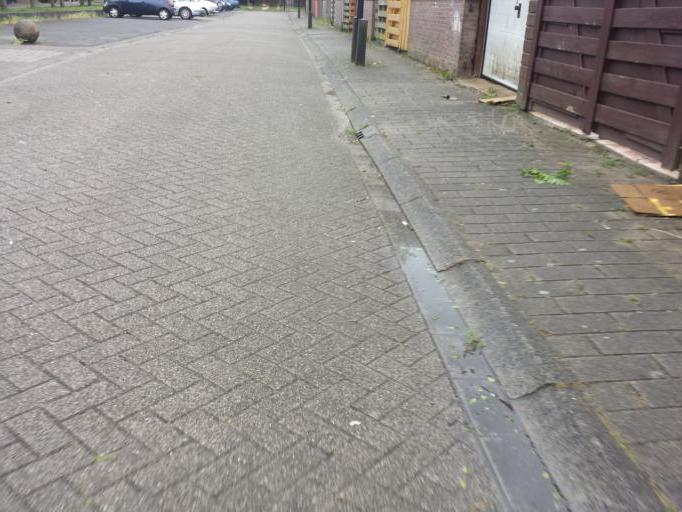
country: NL
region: Flevoland
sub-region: Gemeente Almere
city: Almere Stad
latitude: 52.3953
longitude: 5.2962
